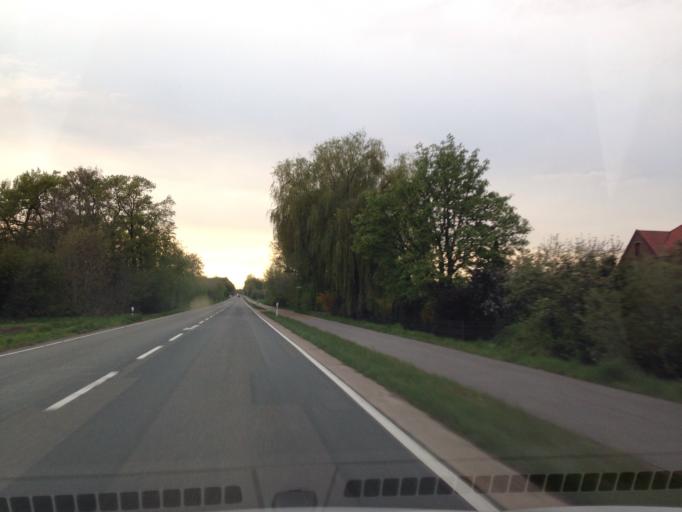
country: DE
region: North Rhine-Westphalia
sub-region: Regierungsbezirk Munster
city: Altenberge
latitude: 52.0629
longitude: 7.4492
